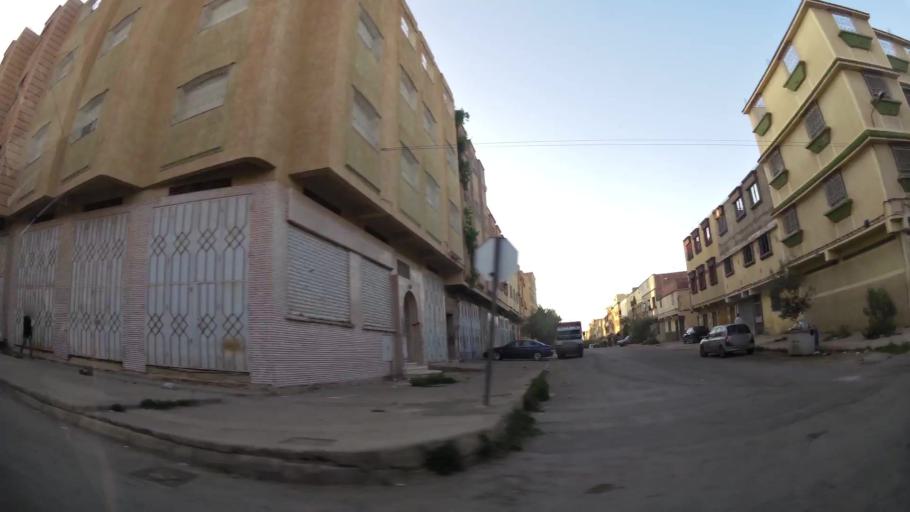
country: MA
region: Oriental
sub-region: Oujda-Angad
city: Oujda
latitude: 34.7068
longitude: -1.9111
